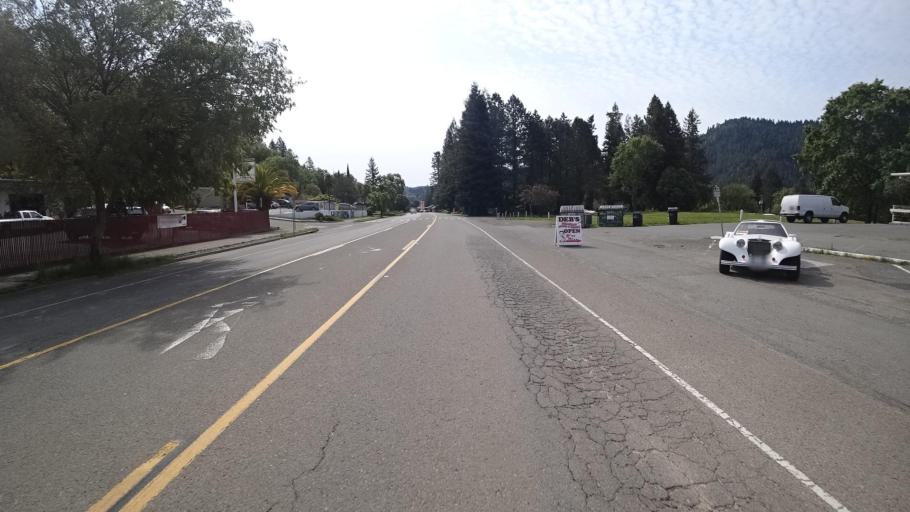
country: US
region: California
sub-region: Humboldt County
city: Redway
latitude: 40.1191
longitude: -123.8219
